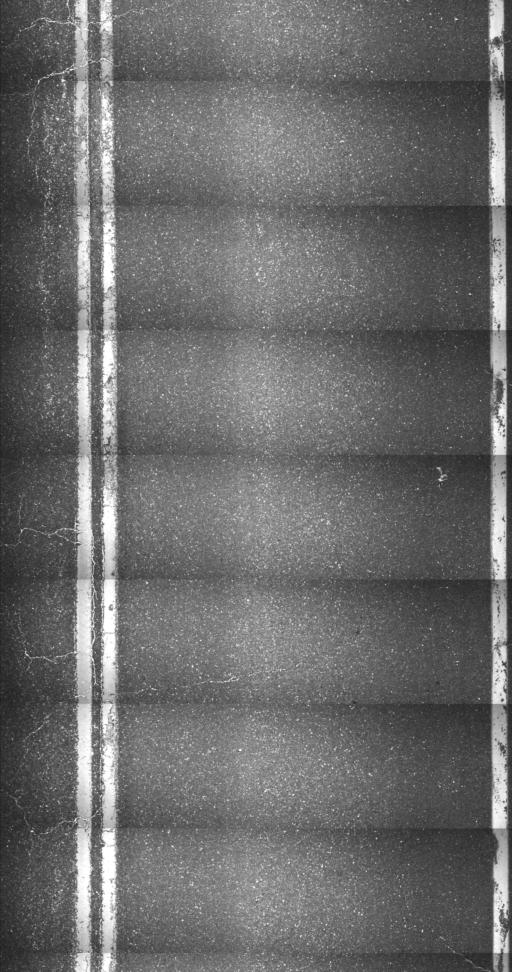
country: US
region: Vermont
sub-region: Windsor County
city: Woodstock
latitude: 43.5579
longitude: -72.7055
